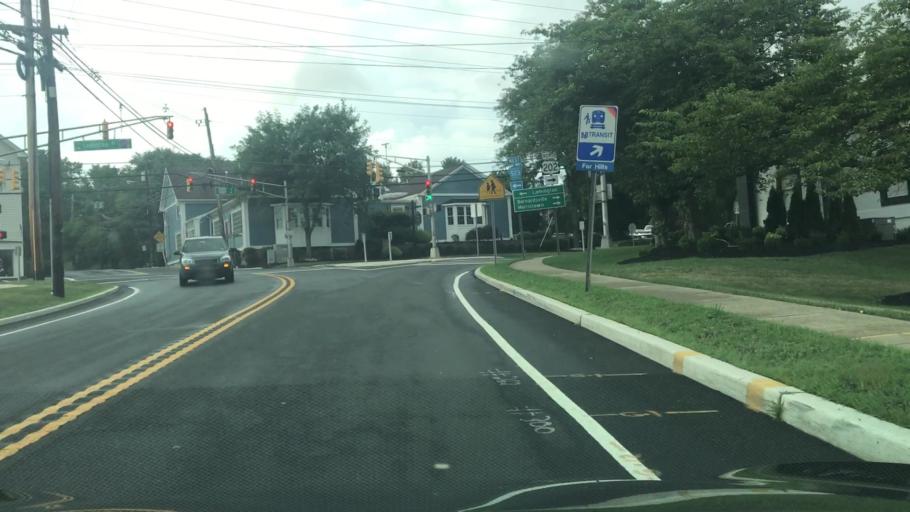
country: US
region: New Jersey
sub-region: Somerset County
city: Bedminster
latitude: 40.6801
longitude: -74.6456
